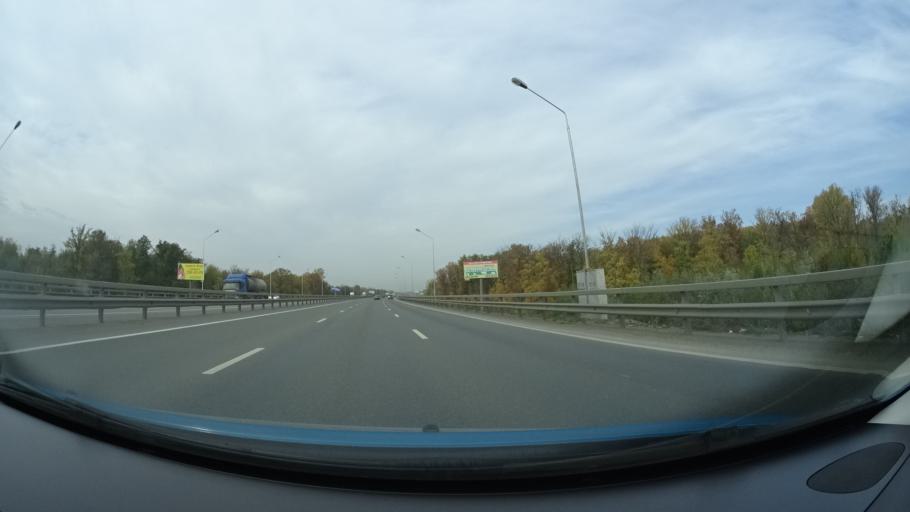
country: RU
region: Bashkortostan
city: Ufa
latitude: 54.6487
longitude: 55.9124
